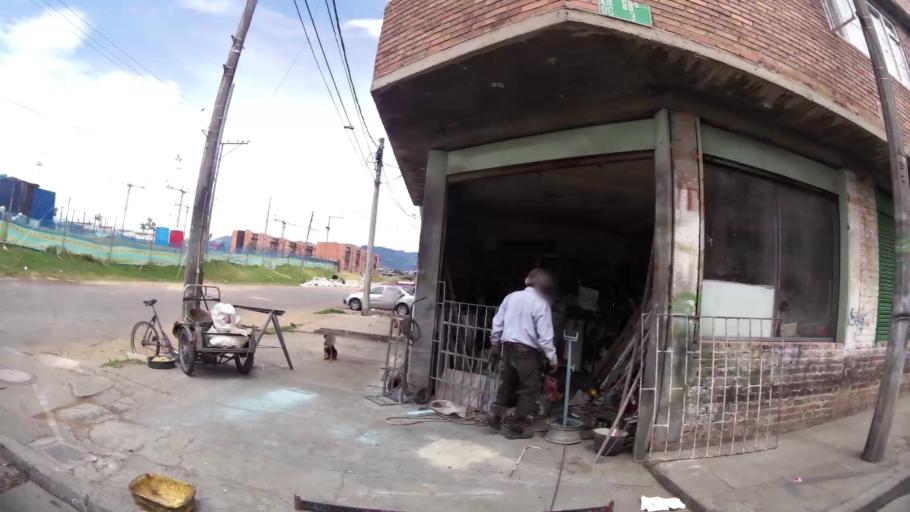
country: CO
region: Bogota D.C.
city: Bogota
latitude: 4.6248
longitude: -74.1276
